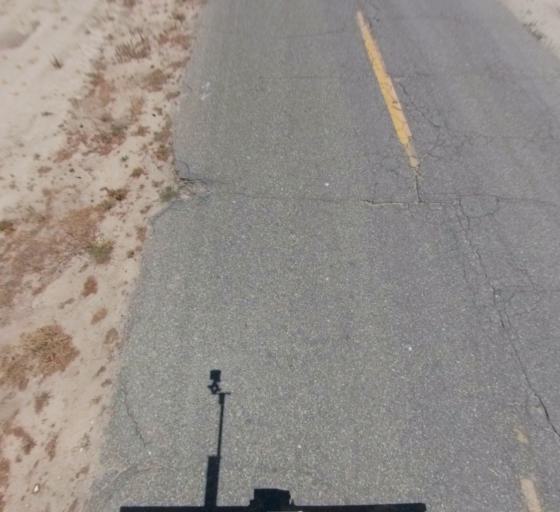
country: US
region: California
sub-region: Madera County
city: Parkwood
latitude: 36.8658
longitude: -120.1043
